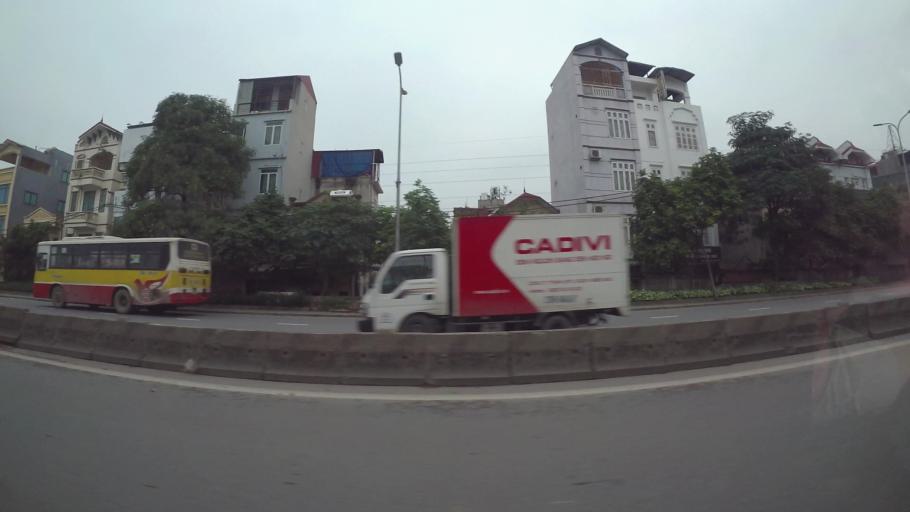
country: VN
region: Ha Noi
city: Hai BaTrung
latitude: 21.0074
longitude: 105.8672
